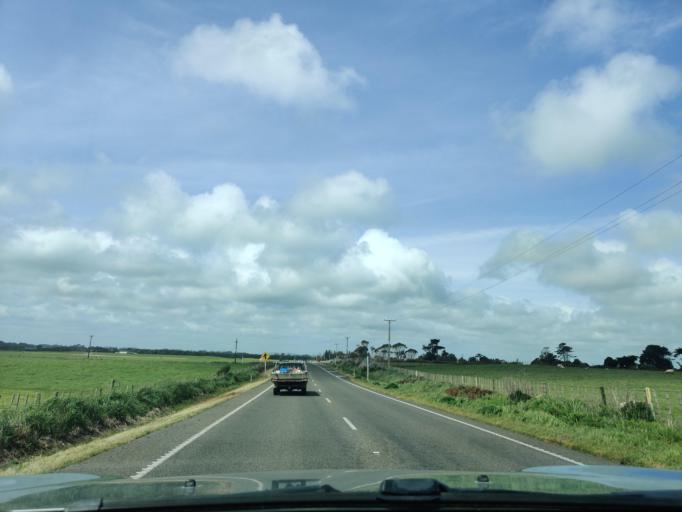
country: NZ
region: Taranaki
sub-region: South Taranaki District
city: Patea
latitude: -39.7677
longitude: 174.6034
